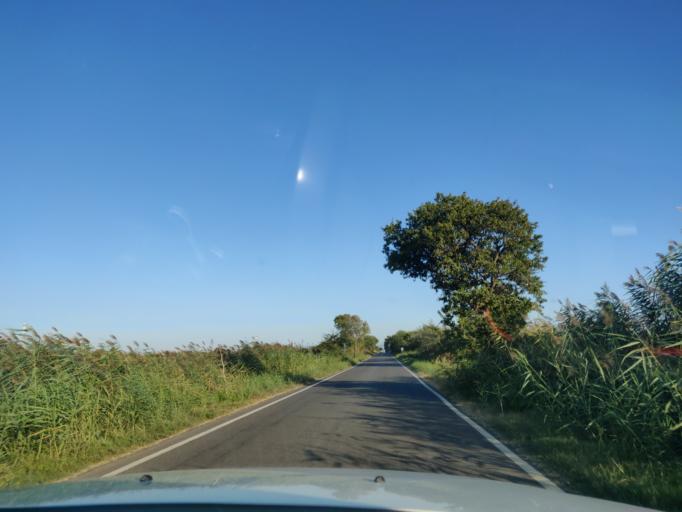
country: IT
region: Latium
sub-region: Provincia di Viterbo
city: Tarquinia
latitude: 42.2719
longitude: 11.6876
